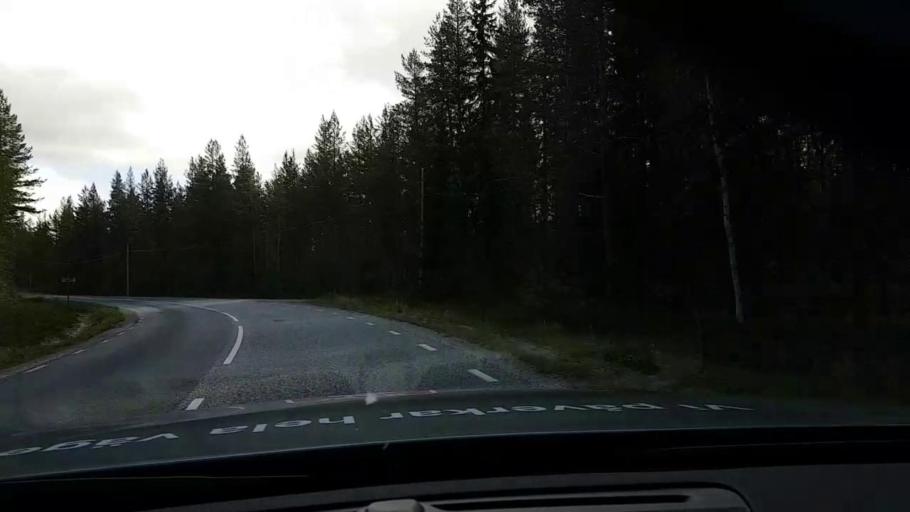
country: SE
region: Vaesterbotten
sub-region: Asele Kommun
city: Asele
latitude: 63.7936
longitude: 17.5769
